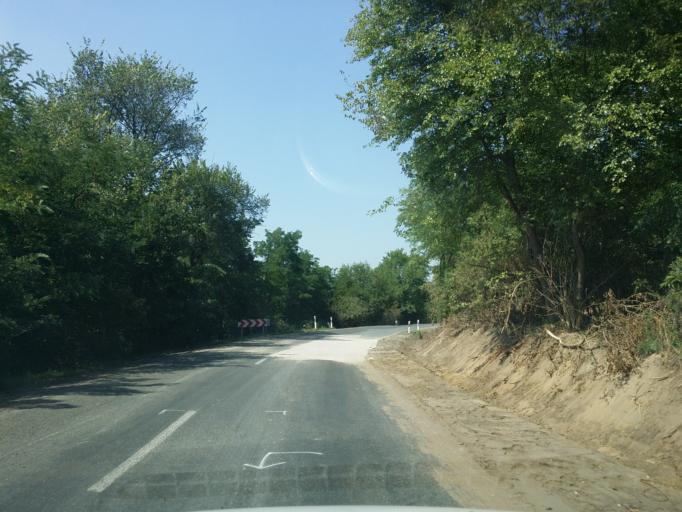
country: HU
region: Tolna
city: Pincehely
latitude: 46.6318
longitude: 18.4136
